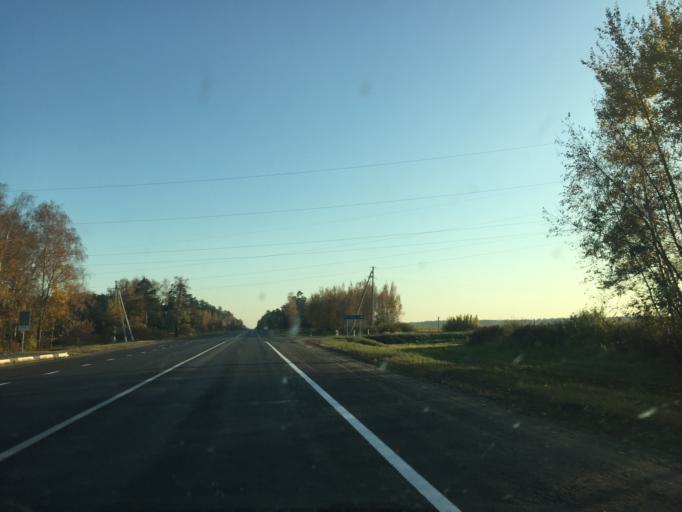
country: BY
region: Mogilev
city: Poselok Voskhod
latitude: 53.7337
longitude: 30.3665
